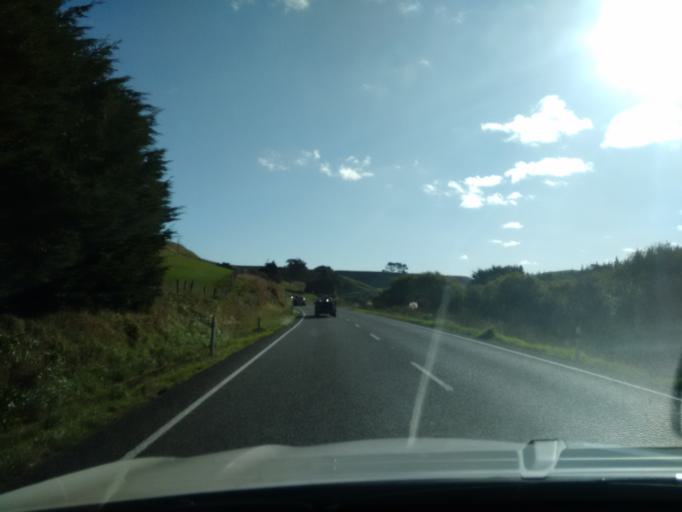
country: NZ
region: Manawatu-Wanganui
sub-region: Wanganui District
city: Wanganui
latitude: -39.8543
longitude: 174.9440
